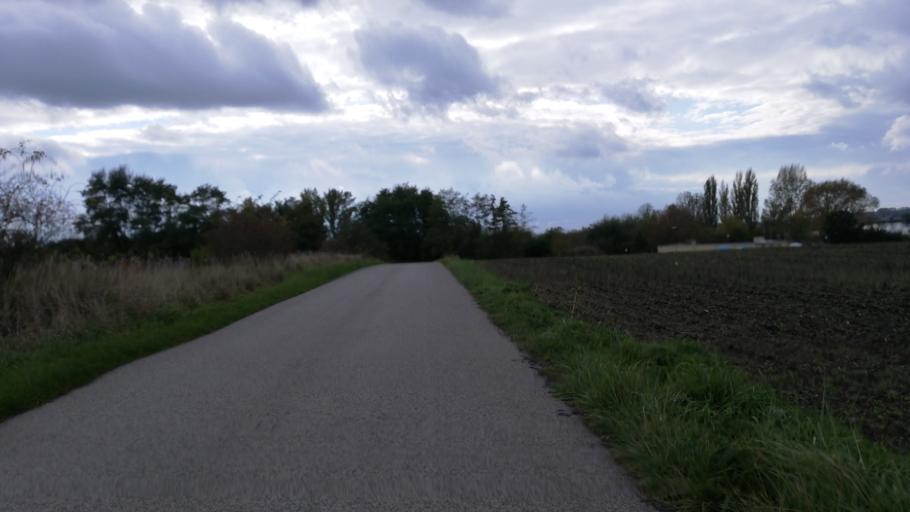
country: SK
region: Trnavsky
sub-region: Okres Skalica
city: Skalica
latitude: 48.8399
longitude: 17.2072
